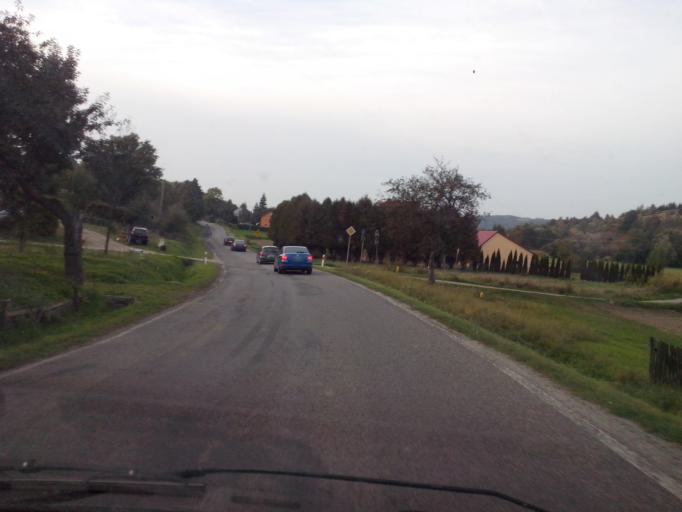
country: PL
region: Subcarpathian Voivodeship
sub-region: Powiat strzyzowski
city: Strzyzow
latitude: 49.8221
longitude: 21.8334
